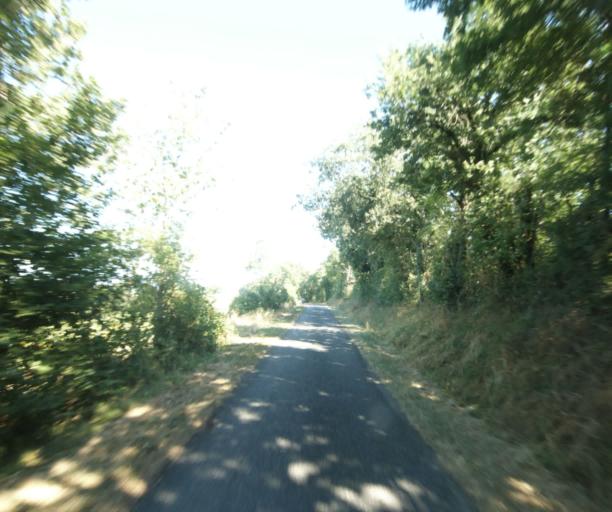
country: FR
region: Midi-Pyrenees
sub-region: Departement de la Haute-Garonne
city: Saint-Felix-Lauragais
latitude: 43.5222
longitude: 1.9096
